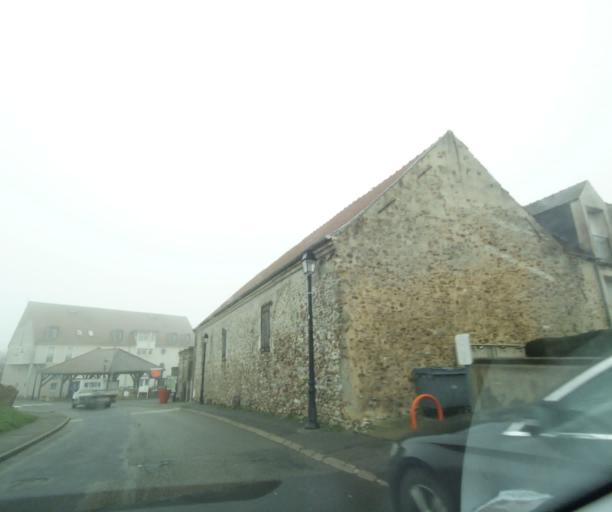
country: FR
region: Ile-de-France
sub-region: Departement de Seine-et-Marne
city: Longperrier
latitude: 49.0527
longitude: 2.6658
